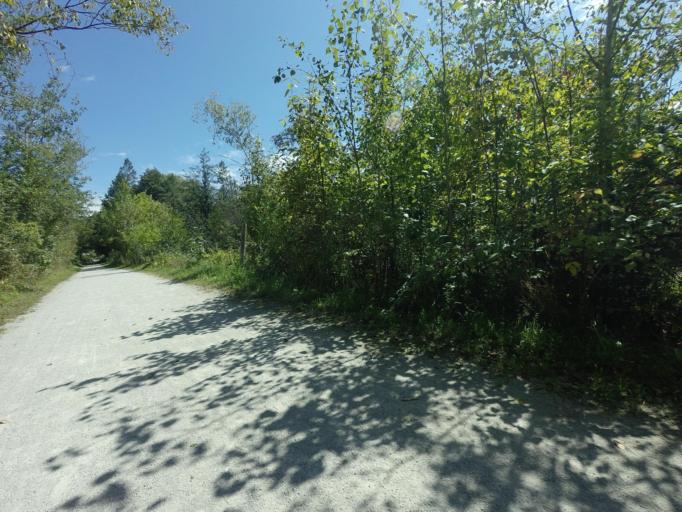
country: CA
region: Ontario
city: Orangeville
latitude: 43.7851
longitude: -80.1459
